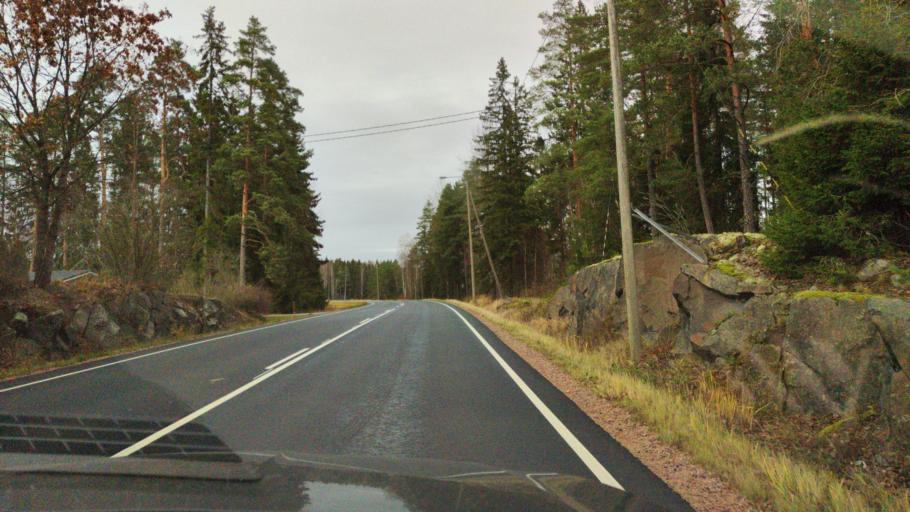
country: FI
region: Varsinais-Suomi
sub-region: Turku
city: Vahto
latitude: 60.6514
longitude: 22.4287
